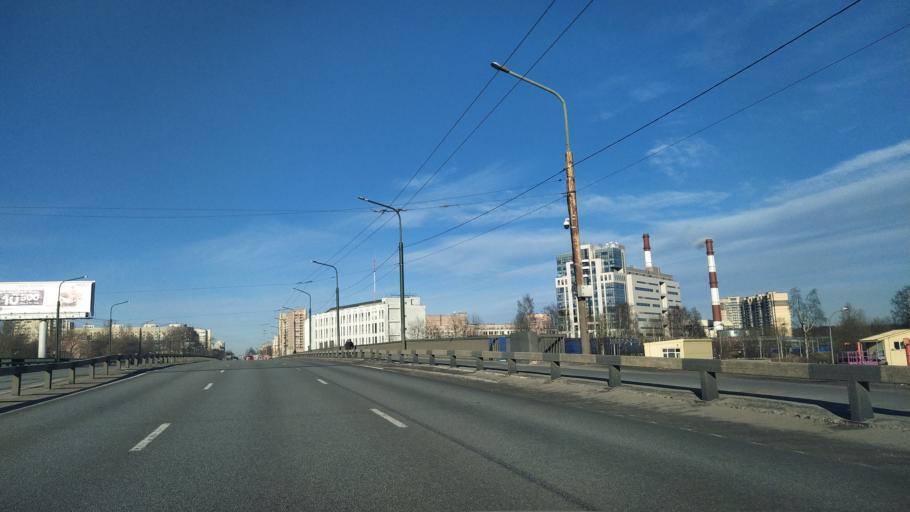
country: RU
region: St.-Petersburg
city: Kushelevka
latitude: 59.9909
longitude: 30.3756
